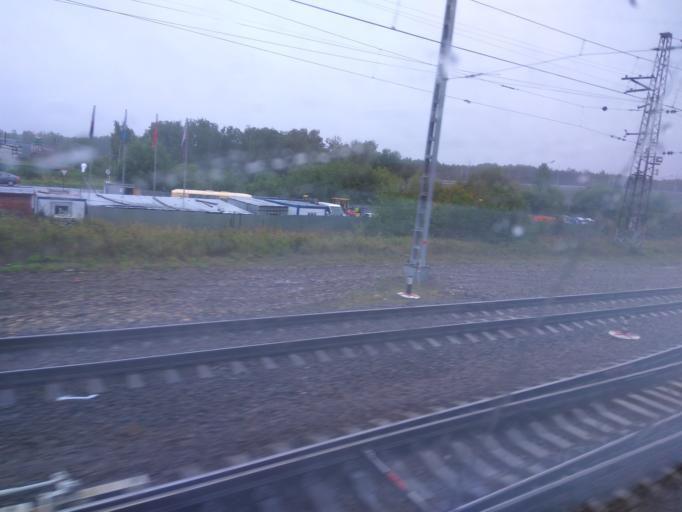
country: RU
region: Moskovskaya
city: Zhilevo
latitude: 54.9923
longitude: 38.0282
